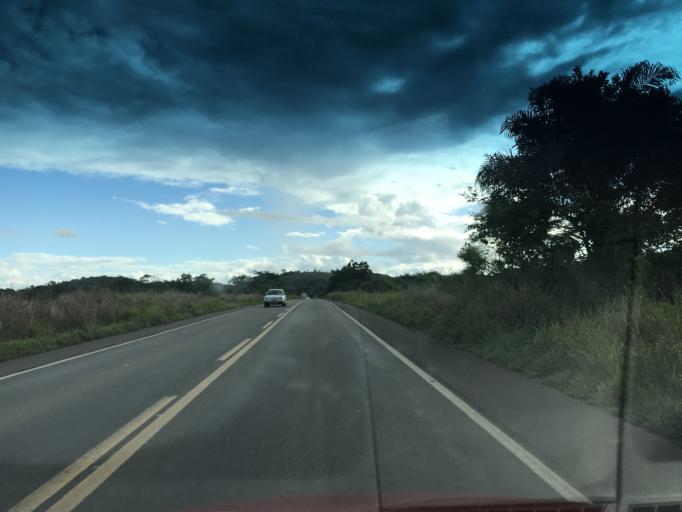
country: BR
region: Bahia
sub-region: Ibirapitanga
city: Ibirapitanga
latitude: -14.1508
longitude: -39.3394
